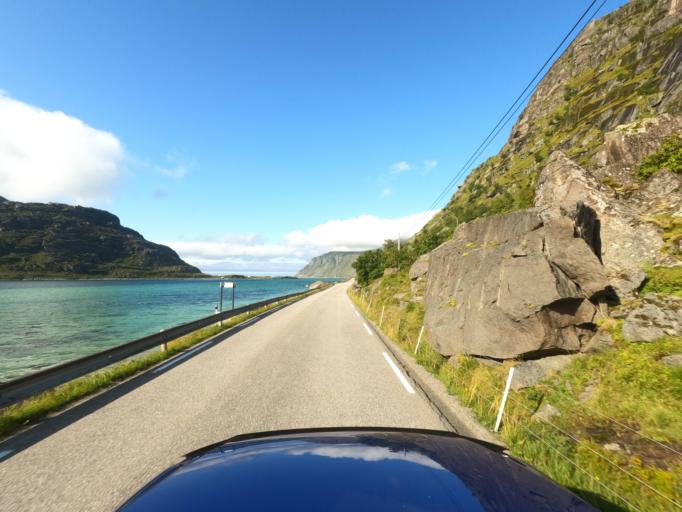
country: NO
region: Nordland
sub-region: Flakstad
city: Ramberg
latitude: 68.0895
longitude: 13.3381
